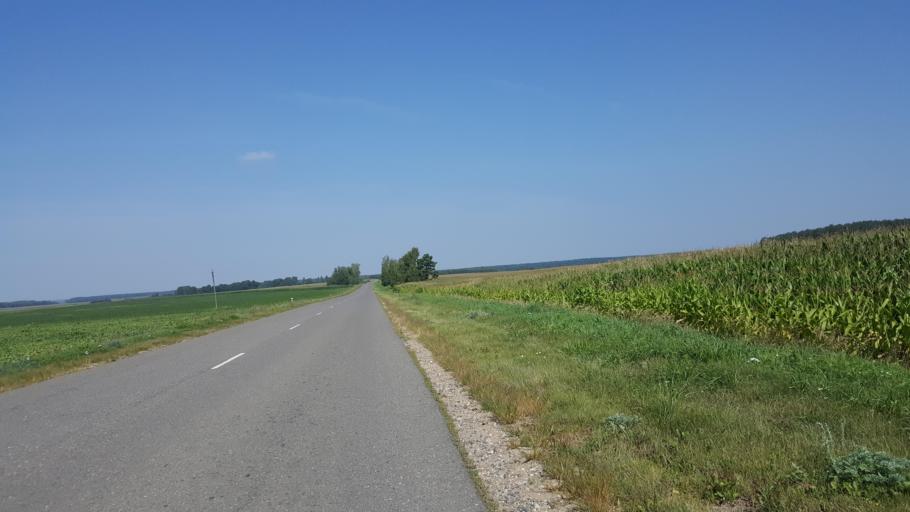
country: BY
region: Brest
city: Kamyanyuki
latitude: 52.4781
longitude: 23.7031
